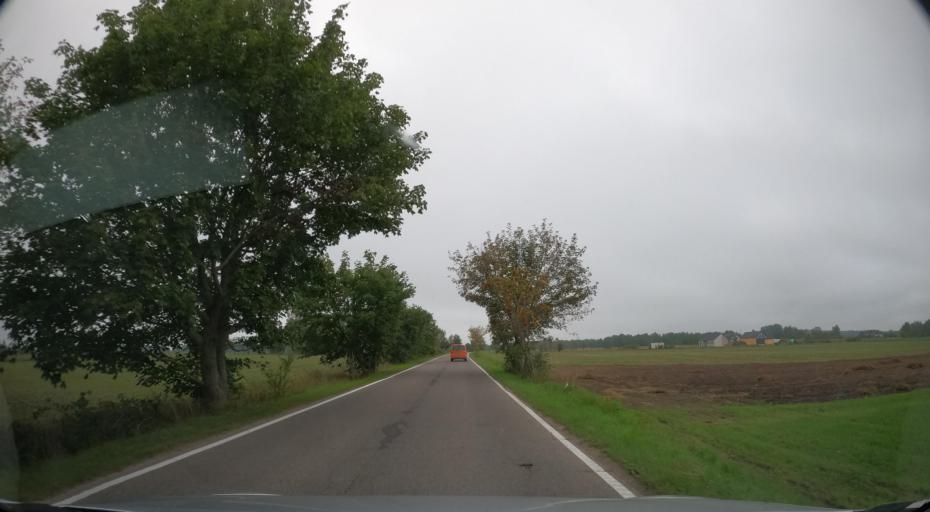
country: PL
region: Pomeranian Voivodeship
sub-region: Powiat wejherowski
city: Szemud
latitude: 54.5023
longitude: 18.1566
